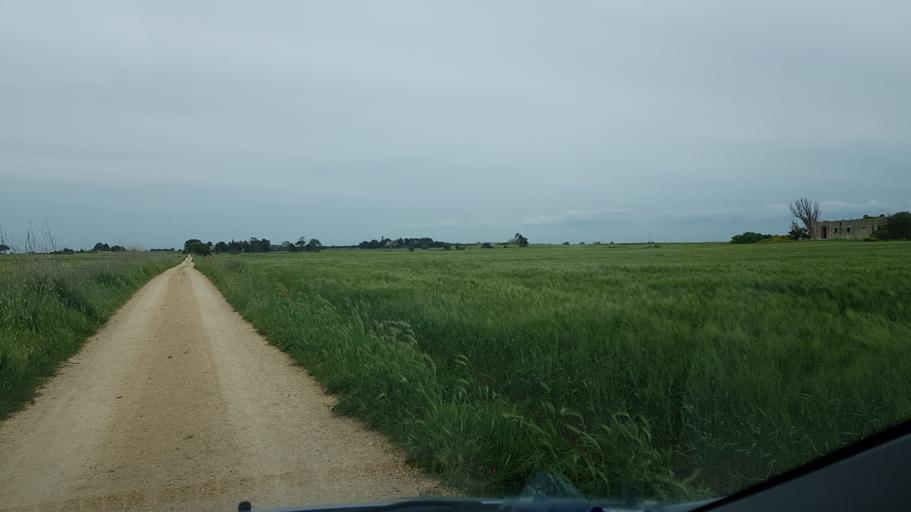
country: IT
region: Apulia
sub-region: Provincia di Brindisi
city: Brindisi
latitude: 40.6569
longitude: 17.8813
